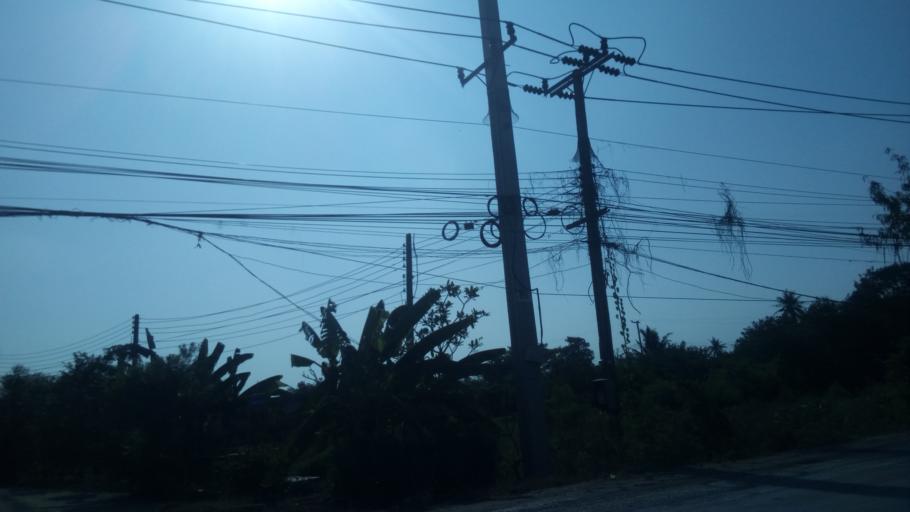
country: TH
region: Nonthaburi
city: Sai Noi
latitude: 13.9313
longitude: 100.3180
